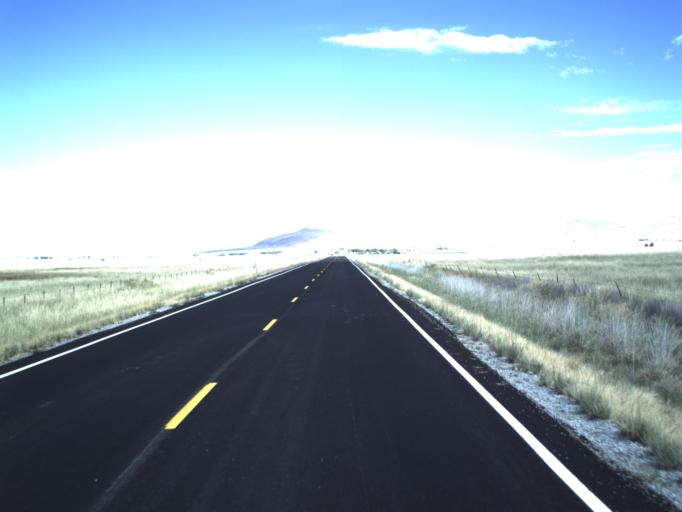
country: US
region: Utah
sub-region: Box Elder County
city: Tremonton
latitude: 41.7455
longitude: -112.4344
